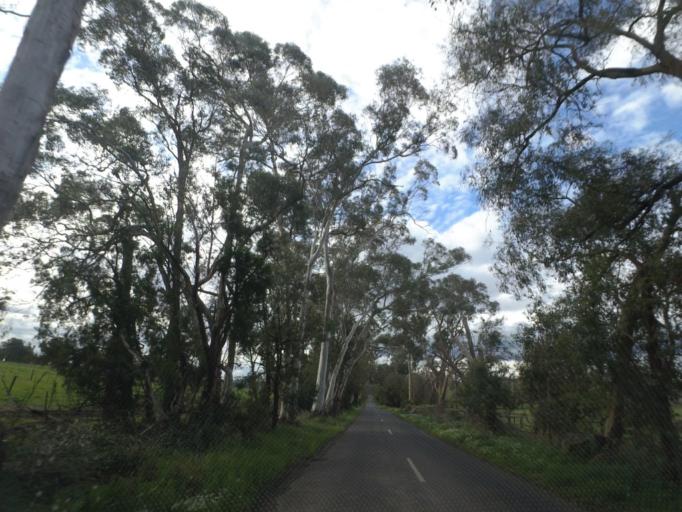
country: AU
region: Victoria
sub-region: Yarra Ranges
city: Mount Evelyn
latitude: -37.7458
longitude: 145.4120
